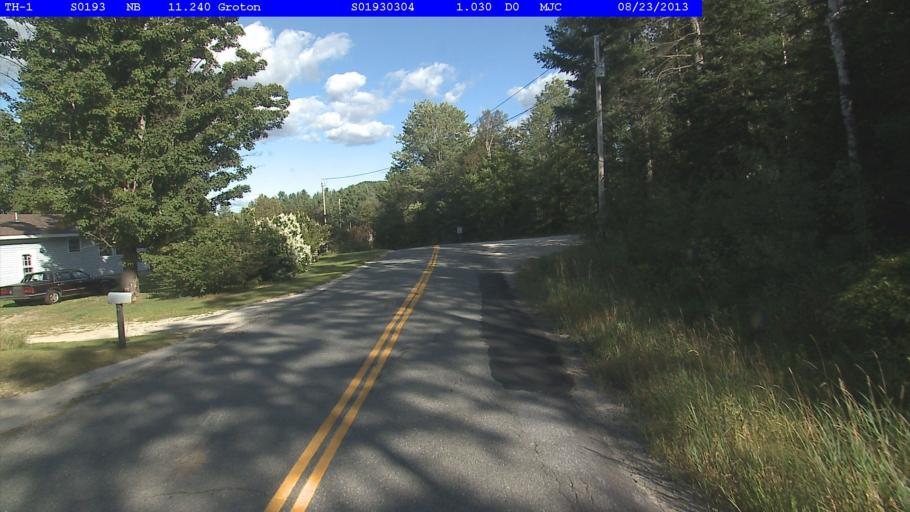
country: US
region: New Hampshire
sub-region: Grafton County
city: Woodsville
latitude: 44.1980
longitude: -72.2069
